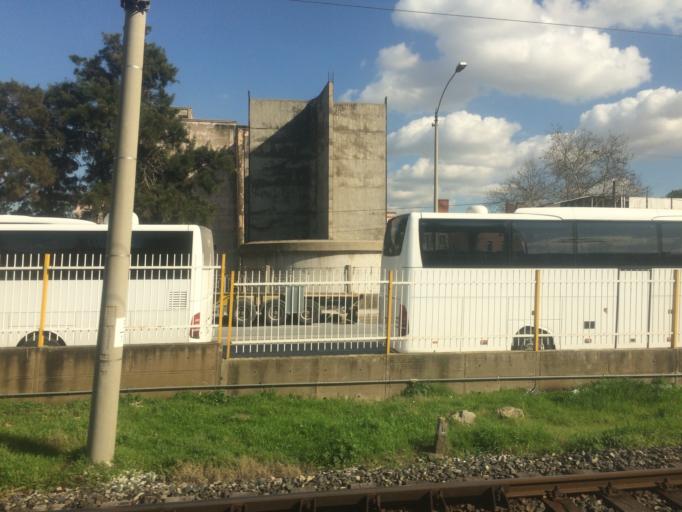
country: TR
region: Izmir
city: Izmir
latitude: 38.4599
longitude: 27.1671
